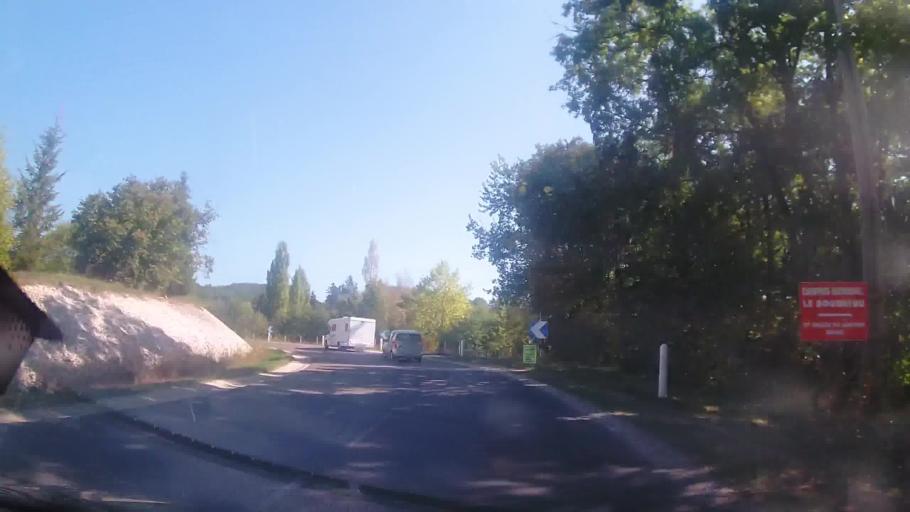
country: FR
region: Aquitaine
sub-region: Departement de la Dordogne
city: Eyvigues-et-Eybenes
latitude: 44.8575
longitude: 1.3423
